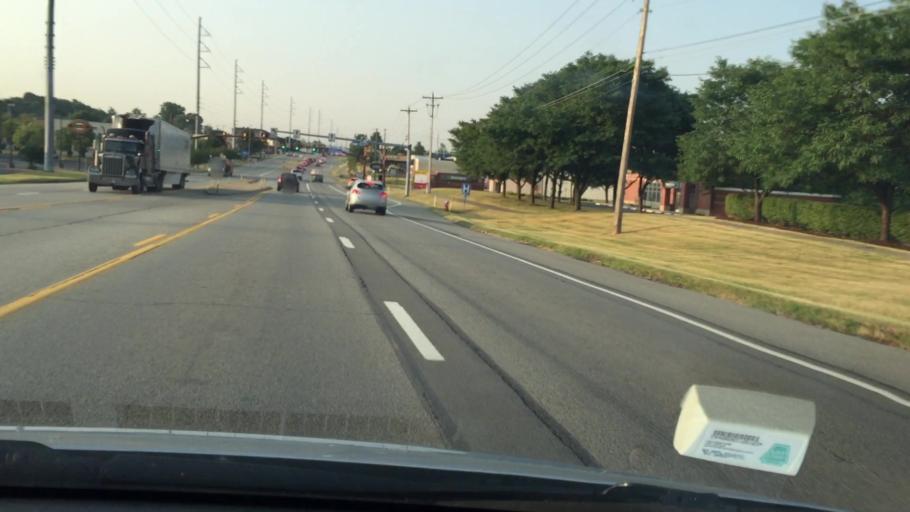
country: US
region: Pennsylvania
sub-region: Butler County
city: Cranberry Township
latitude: 40.6914
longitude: -80.1034
